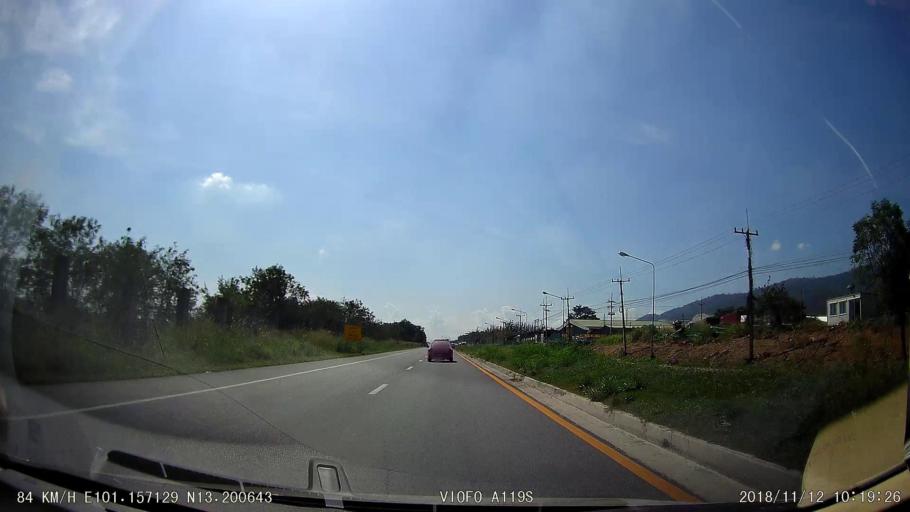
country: TH
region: Chon Buri
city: Ban Bueng
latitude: 13.2001
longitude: 101.1572
